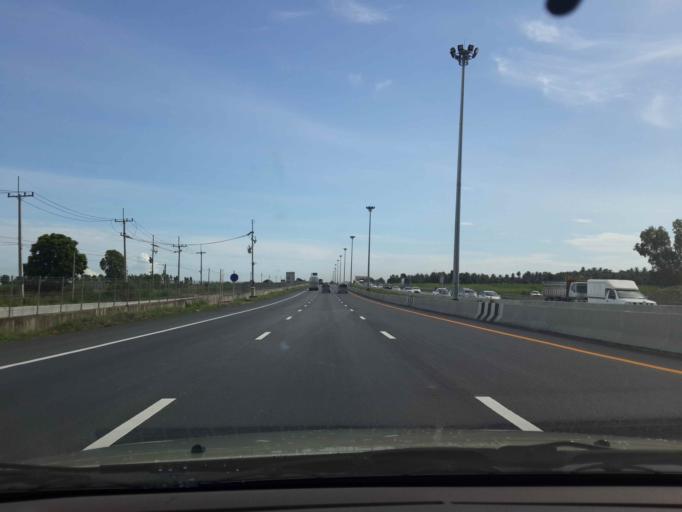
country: TH
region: Chon Buri
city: Ban Talat Bueng
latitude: 13.0249
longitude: 100.9963
